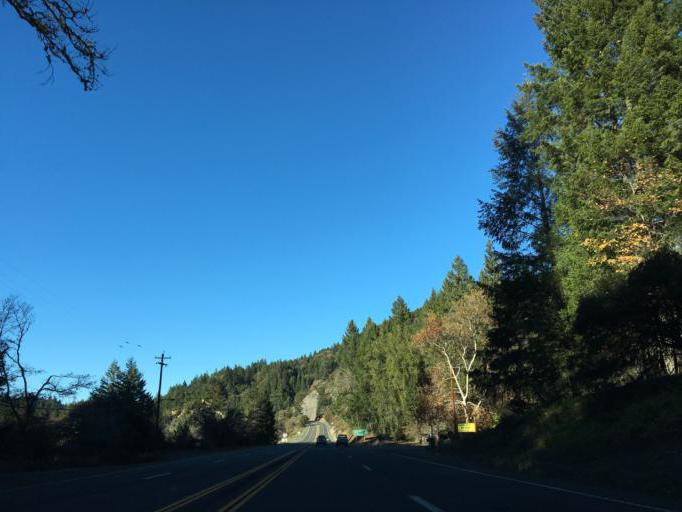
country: US
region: California
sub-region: Mendocino County
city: Brooktrails
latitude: 39.5165
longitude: -123.3907
